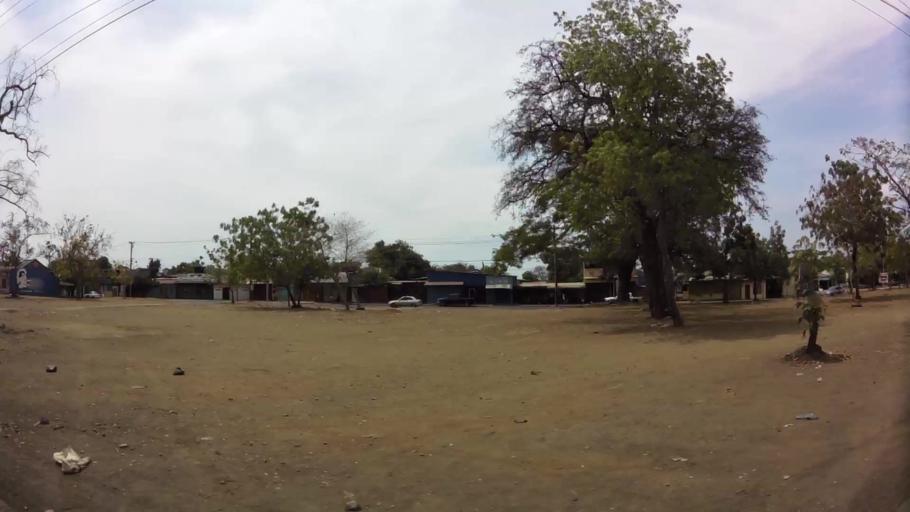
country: NI
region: Managua
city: Managua
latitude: 12.1537
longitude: -86.2633
